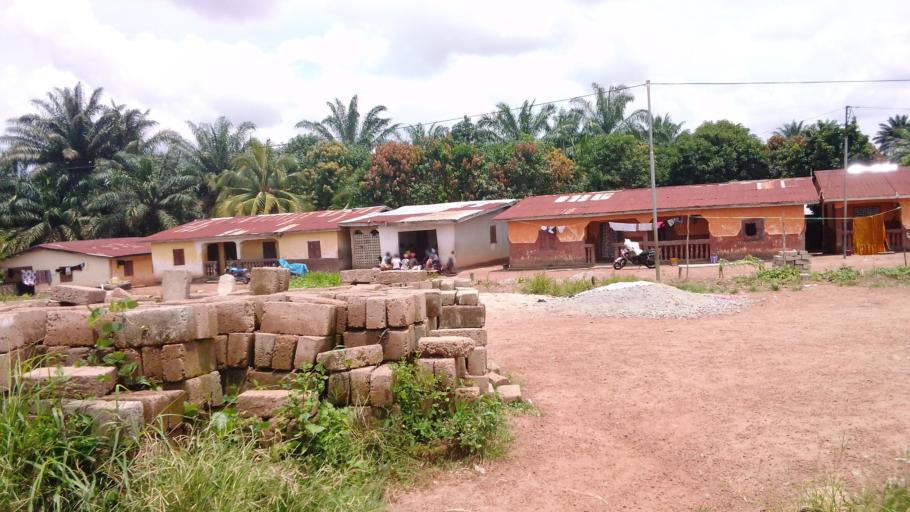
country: SL
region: Northern Province
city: Makeni
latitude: 8.8640
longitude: -12.0377
